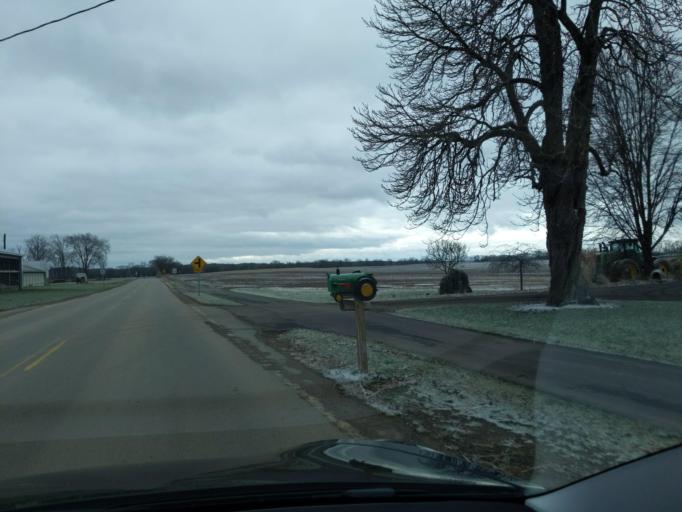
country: US
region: Michigan
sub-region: Jackson County
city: Spring Arbor
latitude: 42.1970
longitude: -84.5536
